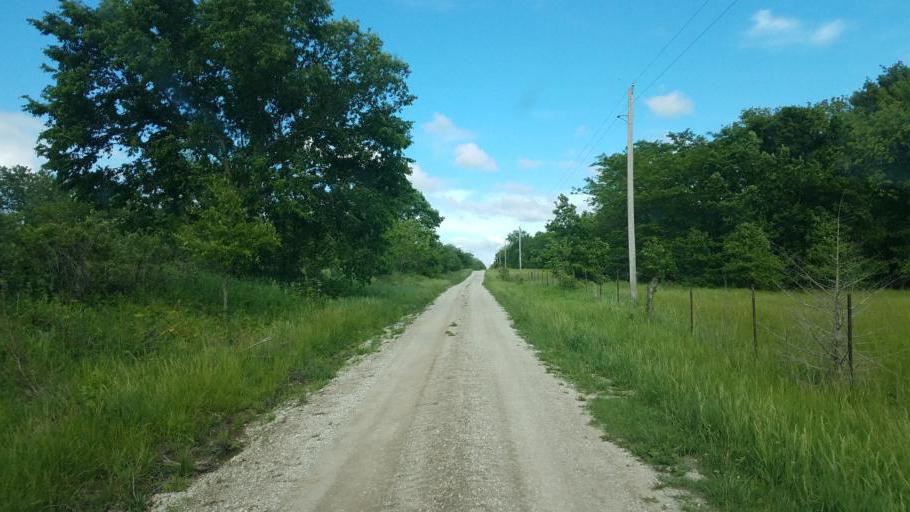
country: US
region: Missouri
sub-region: Mercer County
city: Princeton
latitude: 40.2564
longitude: -93.6878
